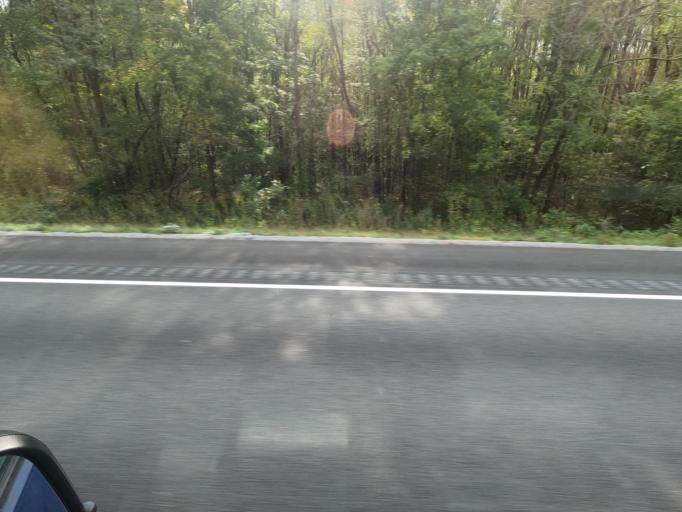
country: US
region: Tennessee
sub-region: Hickman County
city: Centerville
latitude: 35.9008
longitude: -87.6293
